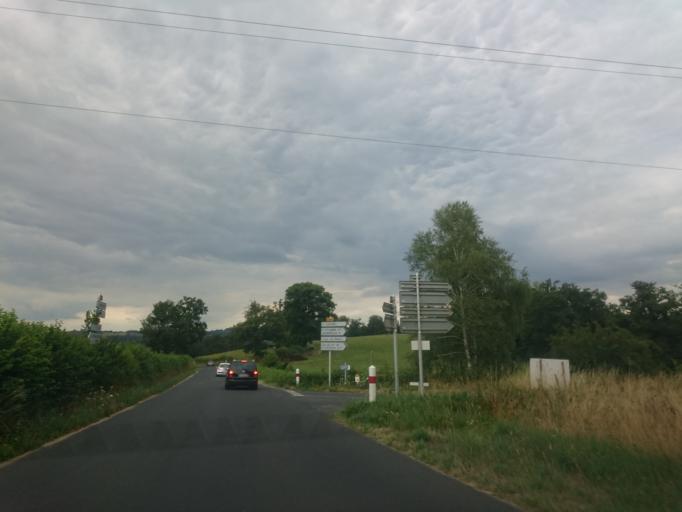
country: FR
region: Auvergne
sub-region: Departement du Cantal
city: Laroquebrou
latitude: 44.9496
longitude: 2.2017
